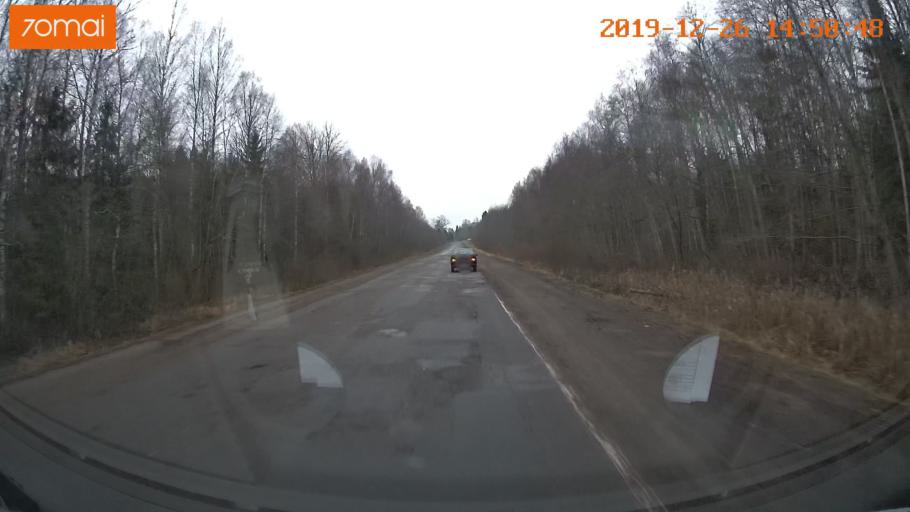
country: RU
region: Jaroslavl
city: Poshekhon'ye
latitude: 58.3293
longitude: 38.9197
